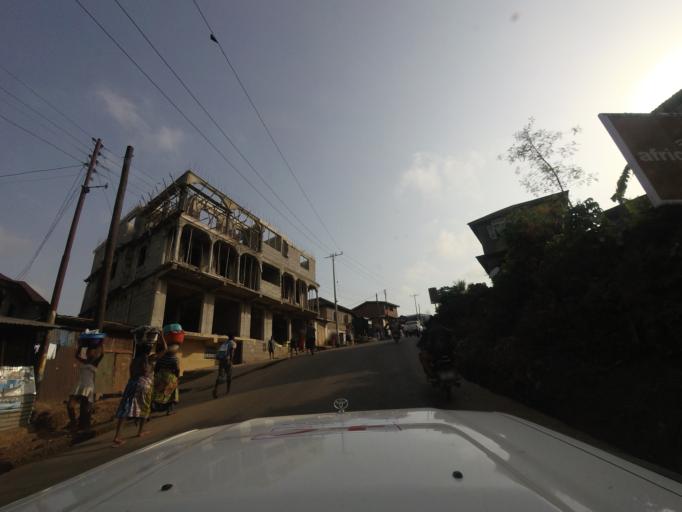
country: SL
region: Western Area
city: Freetown
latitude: 8.4843
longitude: -13.2519
